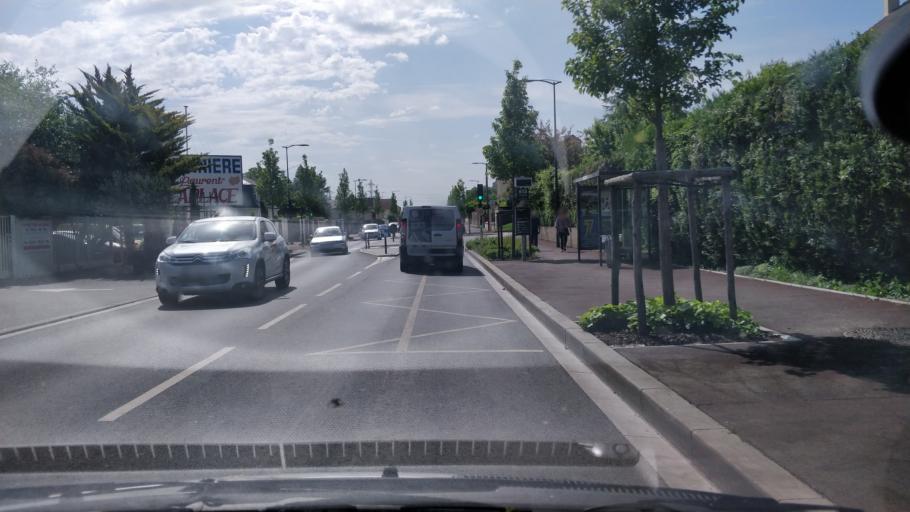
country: FR
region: Ile-de-France
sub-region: Departement de Seine-Saint-Denis
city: Montfermeil
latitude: 48.8900
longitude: 2.5819
